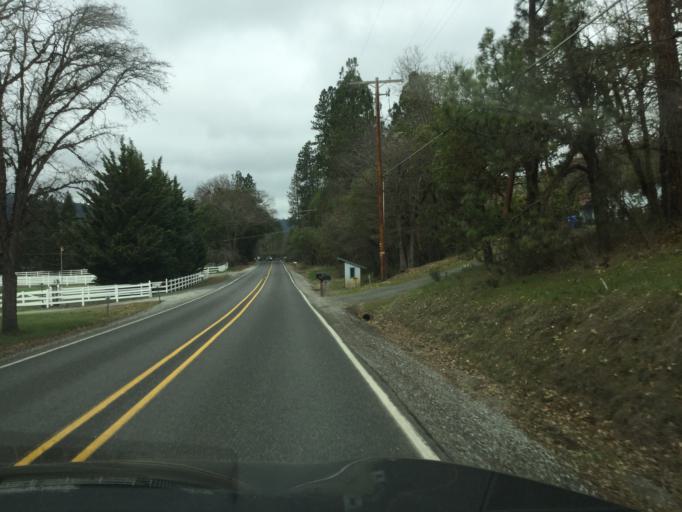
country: US
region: Oregon
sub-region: Jackson County
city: Gold Hill
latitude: 42.3960
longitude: -123.0038
